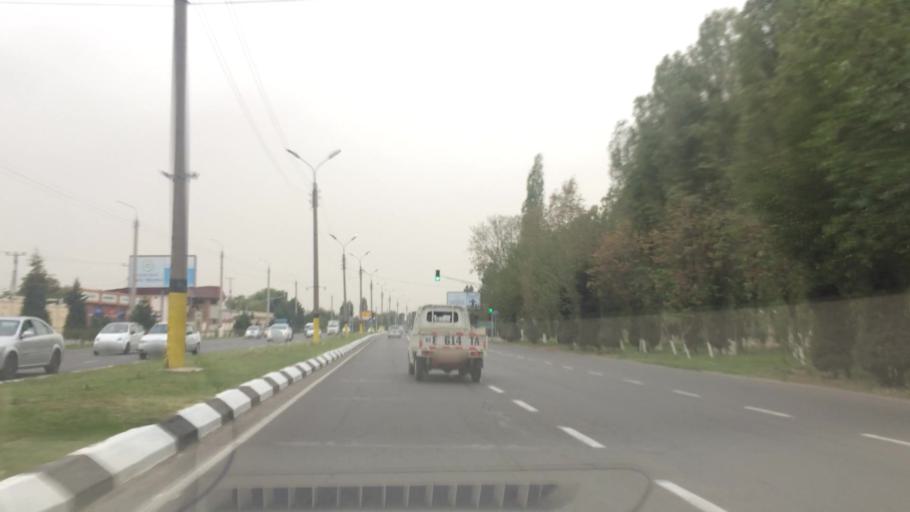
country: UZ
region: Toshkent
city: Salor
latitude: 41.3174
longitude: 69.3567
